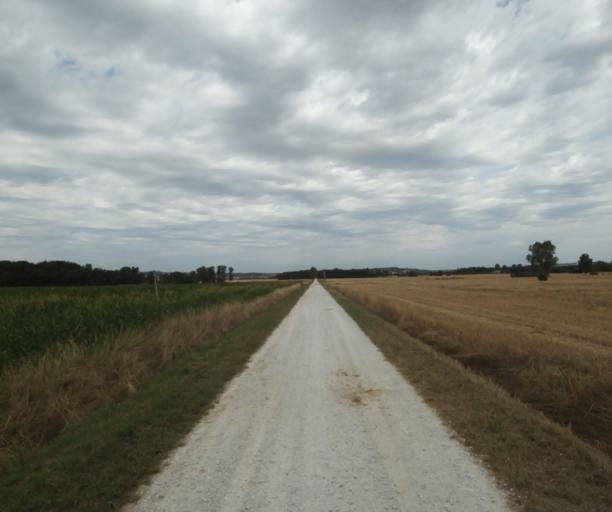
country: FR
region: Midi-Pyrenees
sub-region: Departement de la Haute-Garonne
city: Saint-Felix-Lauragais
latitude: 43.4354
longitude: 1.9456
